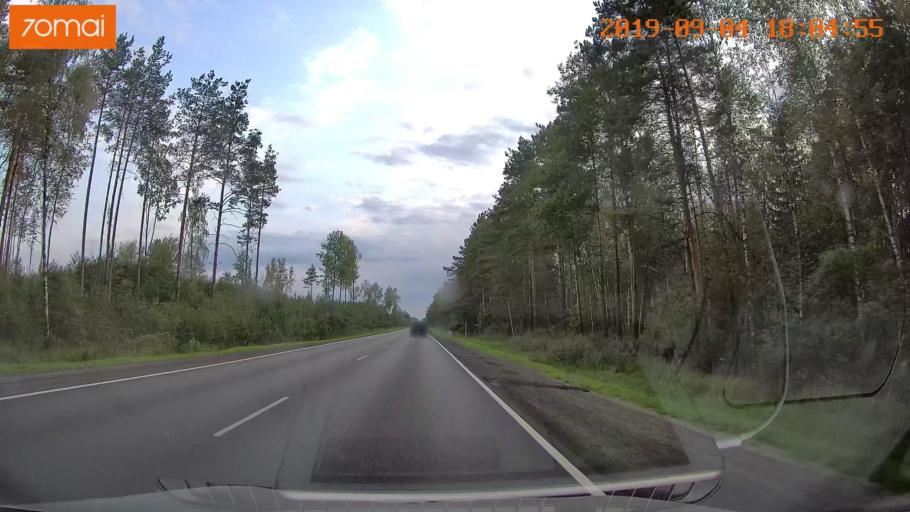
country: RU
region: Moskovskaya
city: Il'inskiy Pogost
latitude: 55.4469
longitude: 38.8330
